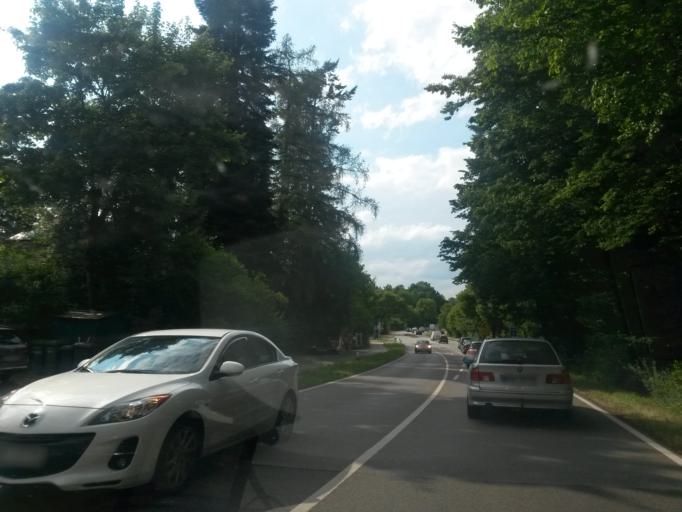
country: DE
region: Bavaria
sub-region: Upper Bavaria
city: Fahrenzhausen
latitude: 48.3426
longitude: 11.5715
